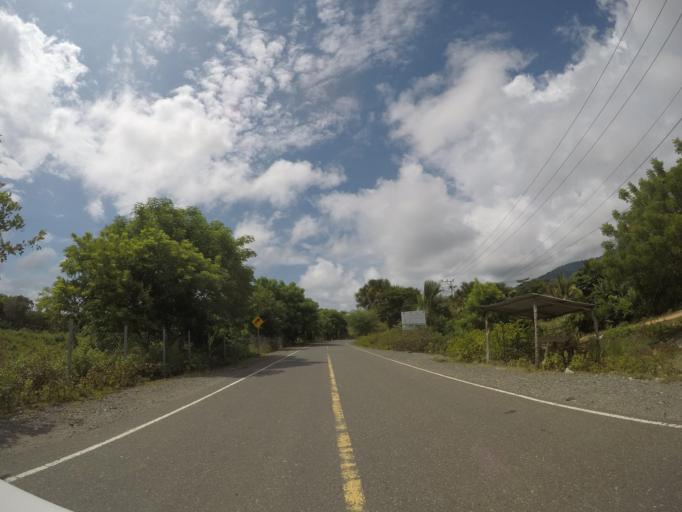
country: TL
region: Liquica
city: Maubara
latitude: -8.7225
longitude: 125.1105
